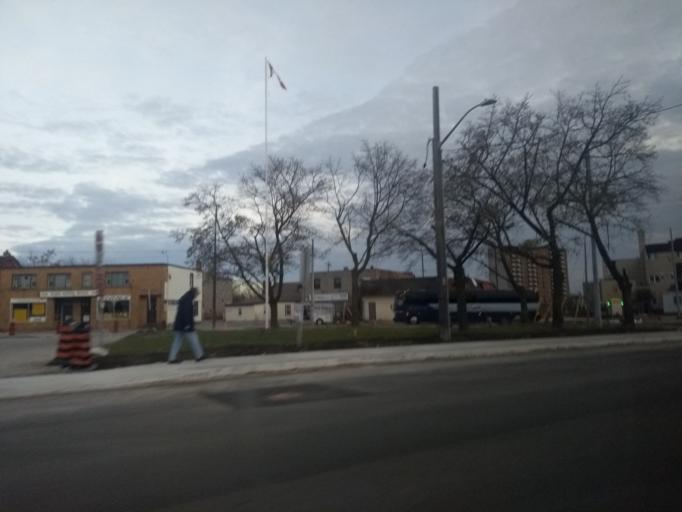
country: CA
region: Ontario
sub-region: Regional Municipality of Niagara
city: St. Catharines
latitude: 43.1628
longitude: -79.2402
